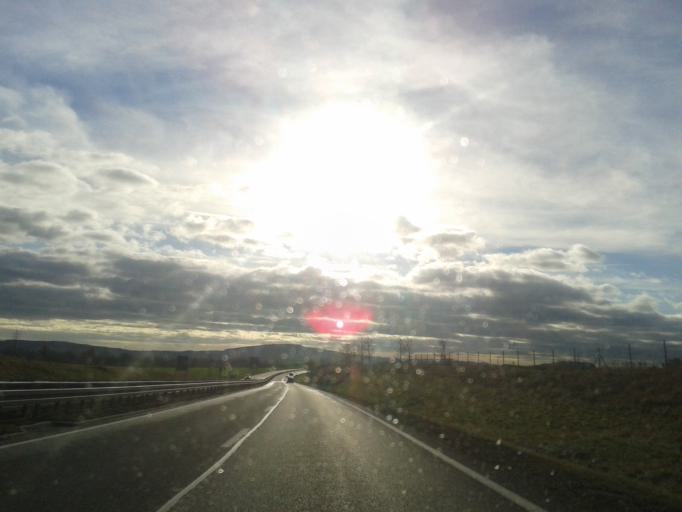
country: DE
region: Saxony
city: Lobau
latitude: 51.1100
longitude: 14.6486
